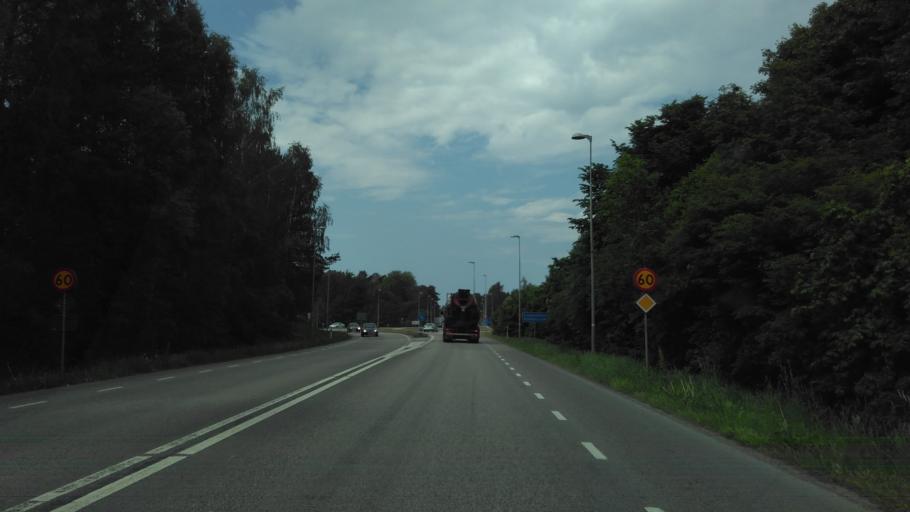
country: SE
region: Vaestra Goetaland
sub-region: Lidkopings Kommun
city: Lidkoping
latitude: 58.4904
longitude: 13.1492
